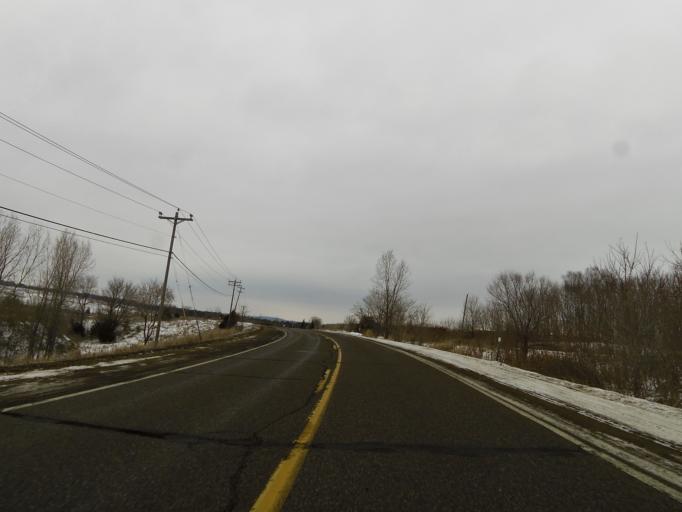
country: US
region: Minnesota
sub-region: Washington County
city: Lakeland
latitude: 44.9491
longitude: -92.8084
